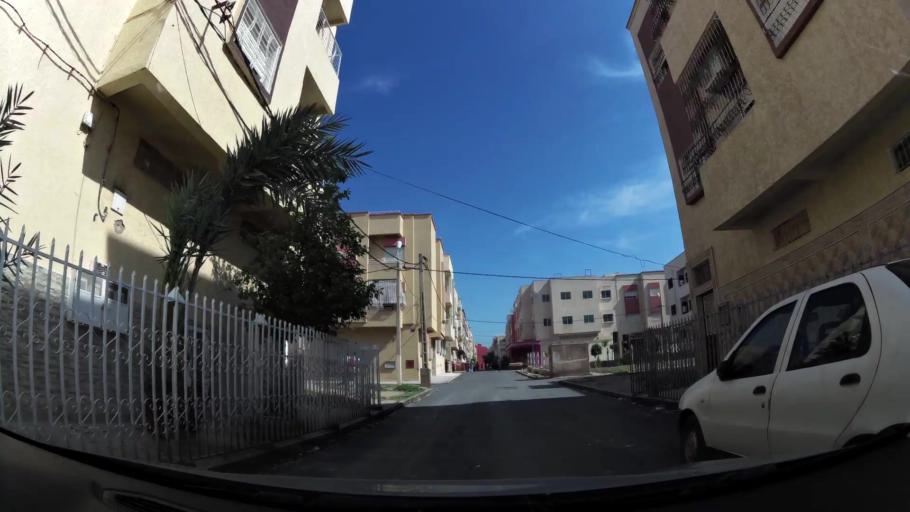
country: MA
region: Fes-Boulemane
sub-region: Fes
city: Fes
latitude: 34.0146
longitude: -5.0374
